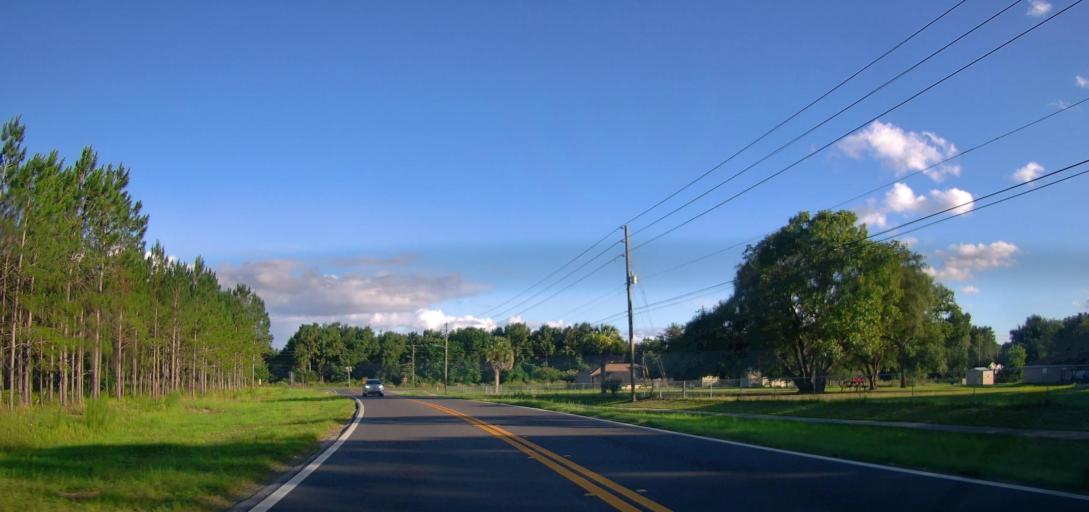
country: US
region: Florida
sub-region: Marion County
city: Silver Springs Shores
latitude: 29.0678
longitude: -82.0077
